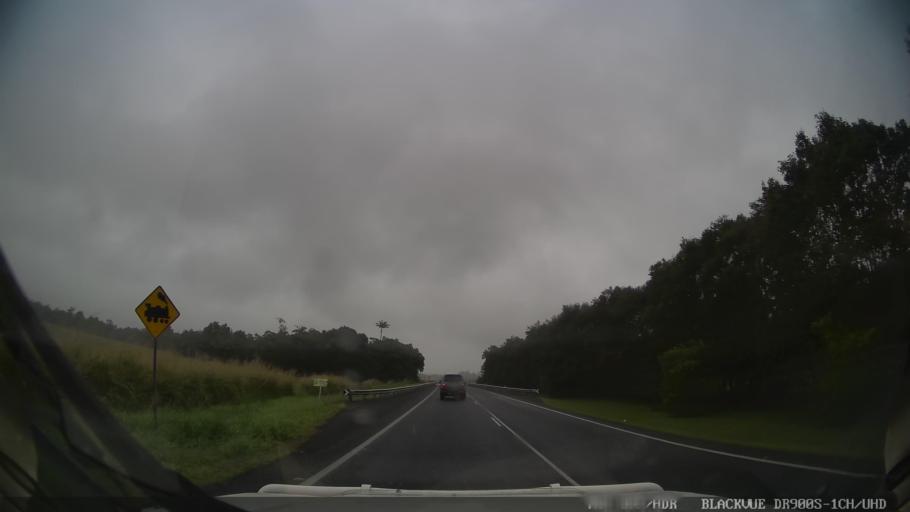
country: AU
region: Queensland
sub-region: Cassowary Coast
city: Innisfail
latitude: -17.6500
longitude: 146.0332
